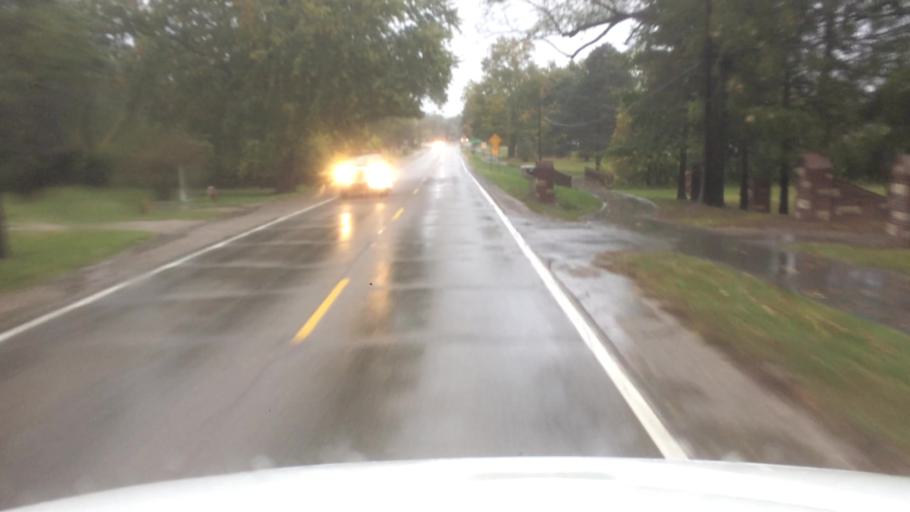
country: US
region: Michigan
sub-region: Oakland County
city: Oxford
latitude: 42.7841
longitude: -83.3152
